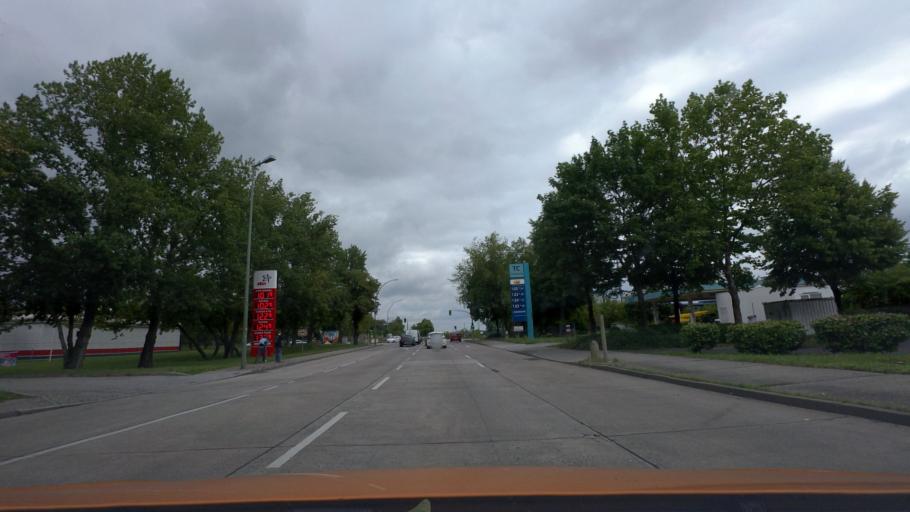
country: DE
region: Berlin
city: Neu-Hohenschoenhausen
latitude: 52.5564
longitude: 13.5272
